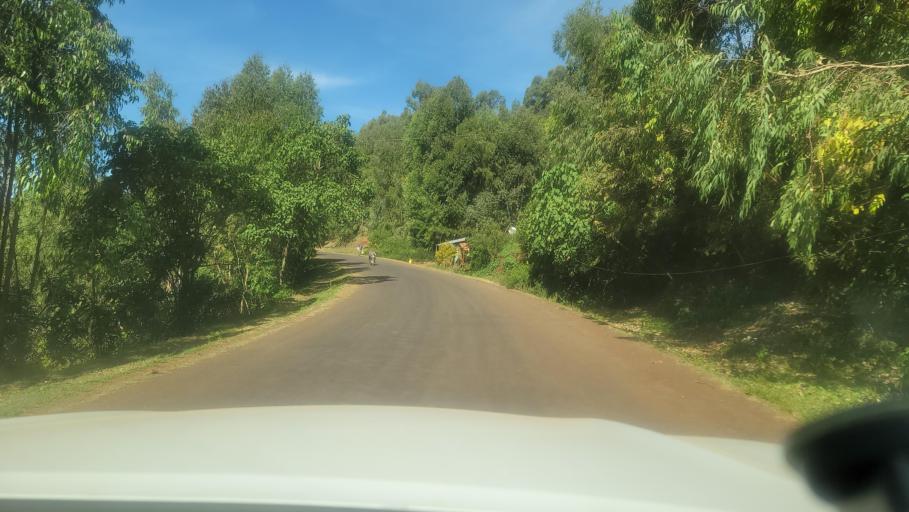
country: ET
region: Oromiya
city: Agaro
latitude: 7.7995
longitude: 36.4759
